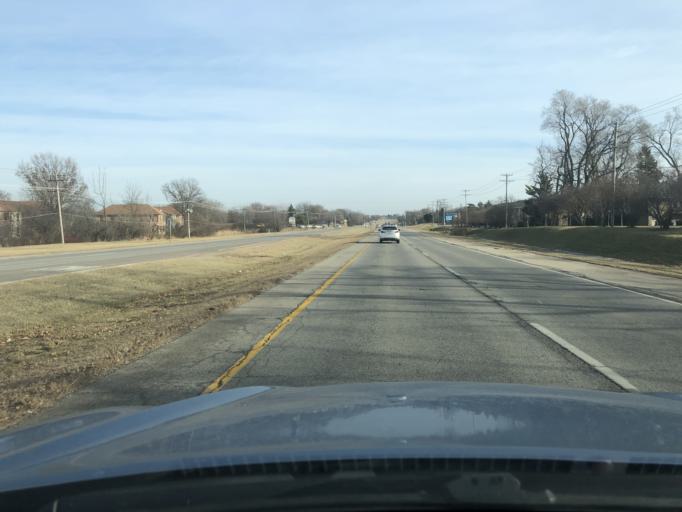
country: US
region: Illinois
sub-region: Cook County
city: South Barrington
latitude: 42.0542
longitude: -88.1243
